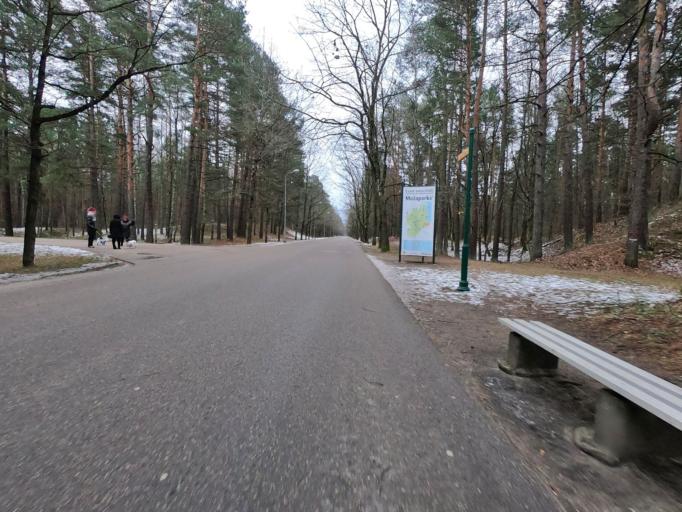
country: LV
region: Riga
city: Jaunciems
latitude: 57.0181
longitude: 24.1411
